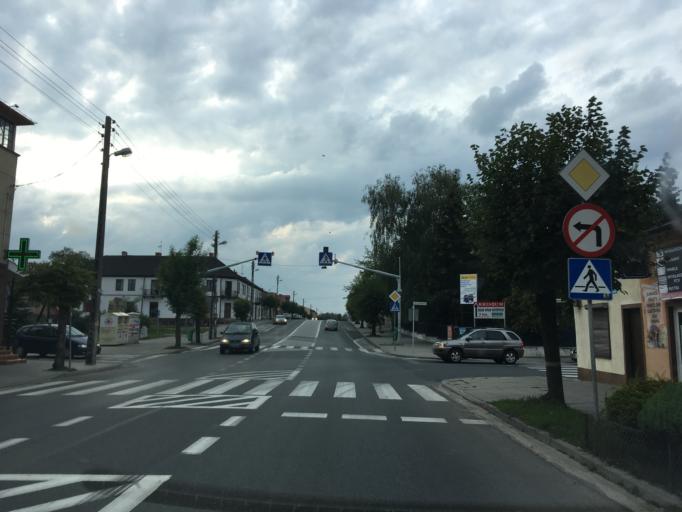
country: PL
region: Lodz Voivodeship
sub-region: Powiat radomszczanski
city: Przedborz
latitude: 51.0896
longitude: 19.8693
